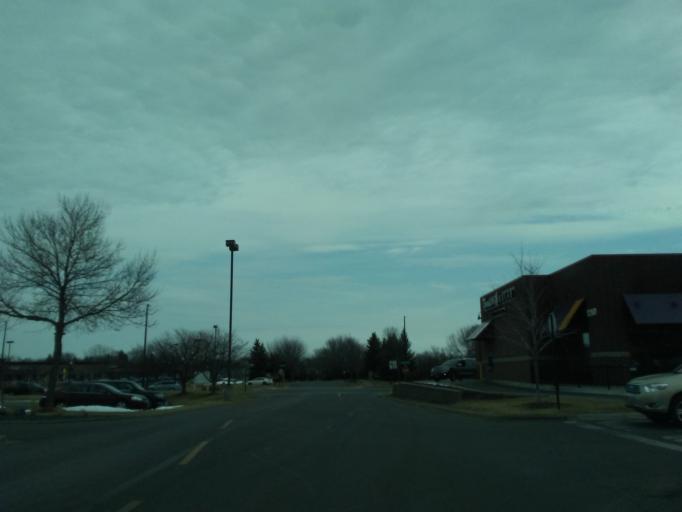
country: US
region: Minnesota
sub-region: Dakota County
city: Eagan
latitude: 44.8349
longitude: -93.1542
